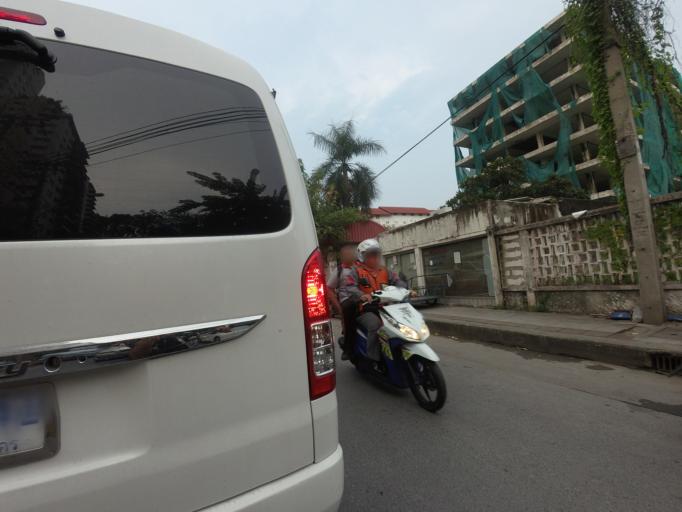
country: TH
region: Bangkok
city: Watthana
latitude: 13.7430
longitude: 100.5637
